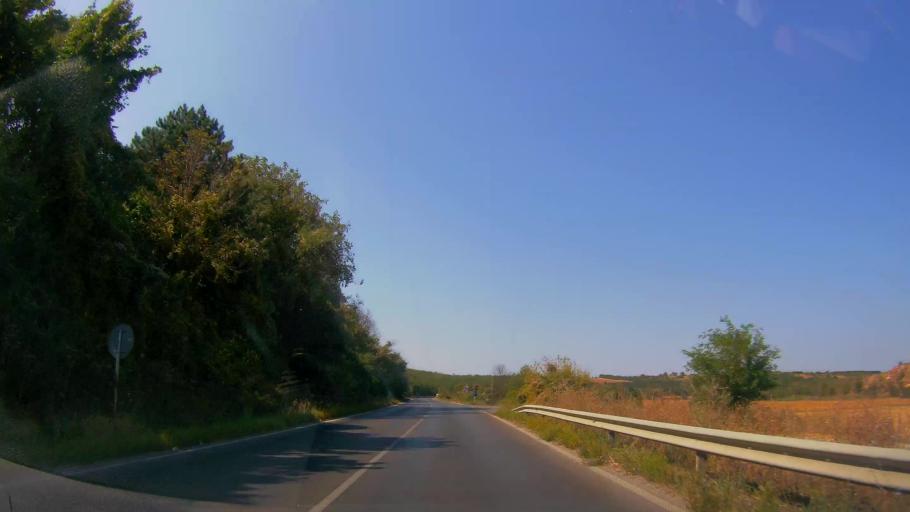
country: BG
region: Razgrad
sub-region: Obshtina Tsar Kaloyan
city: Tsar Kaloyan
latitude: 43.6143
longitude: 26.2190
